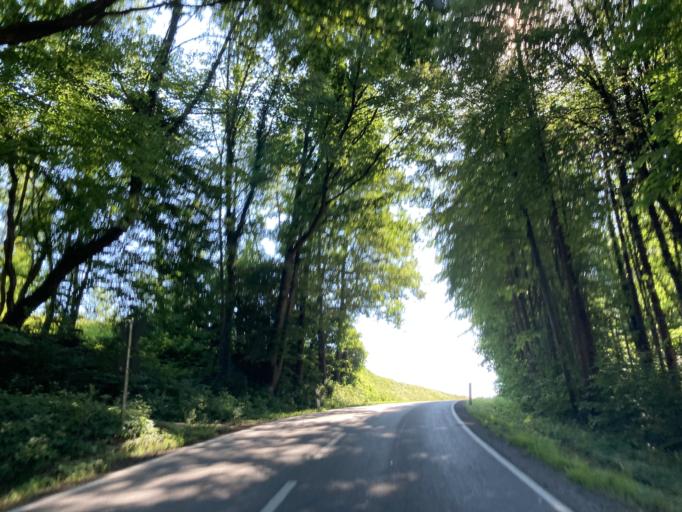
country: DE
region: Bavaria
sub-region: Upper Bavaria
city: Bad Endorf
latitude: 47.9268
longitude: 12.2907
